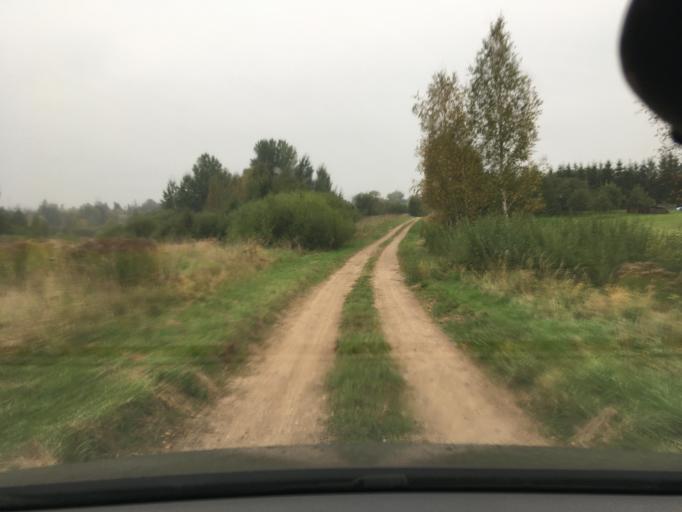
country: LV
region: Kuldigas Rajons
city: Kuldiga
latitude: 56.9883
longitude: 22.0261
